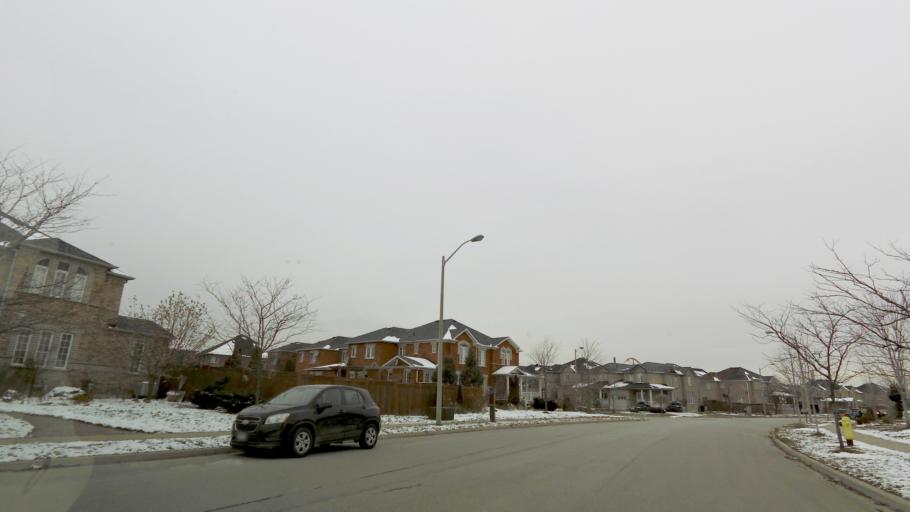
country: CA
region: Ontario
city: Vaughan
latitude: 43.8311
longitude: -79.5399
